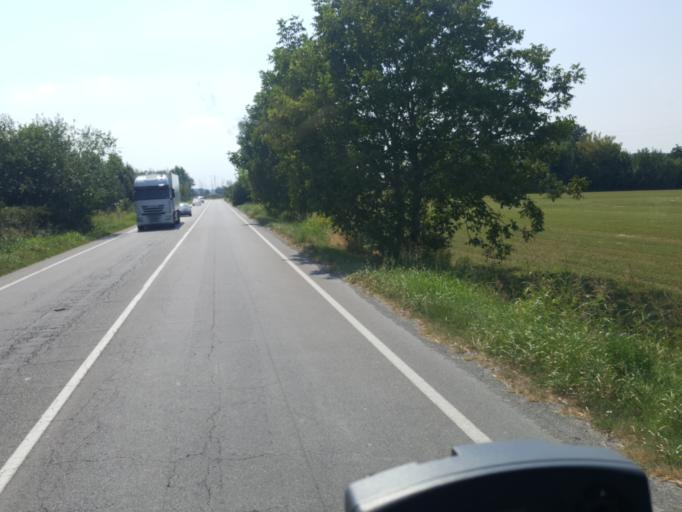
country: IT
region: Emilia-Romagna
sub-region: Provincia di Piacenza
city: Monticelli d'Ongina
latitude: 45.0741
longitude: 9.9010
